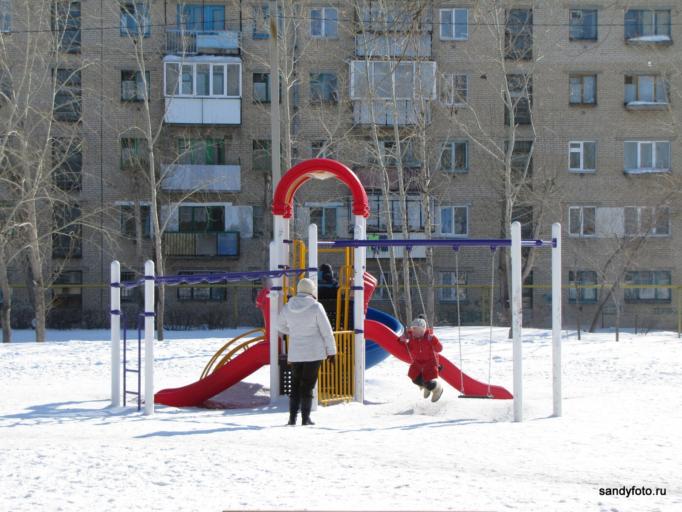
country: RU
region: Chelyabinsk
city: Troitsk
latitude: 54.0799
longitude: 61.5334
